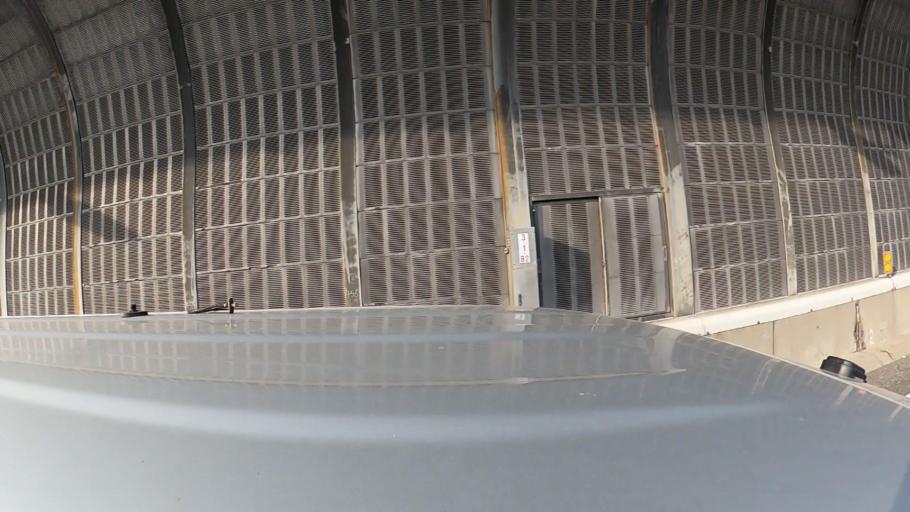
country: JP
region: Saitama
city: Wako
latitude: 35.7623
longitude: 139.5945
